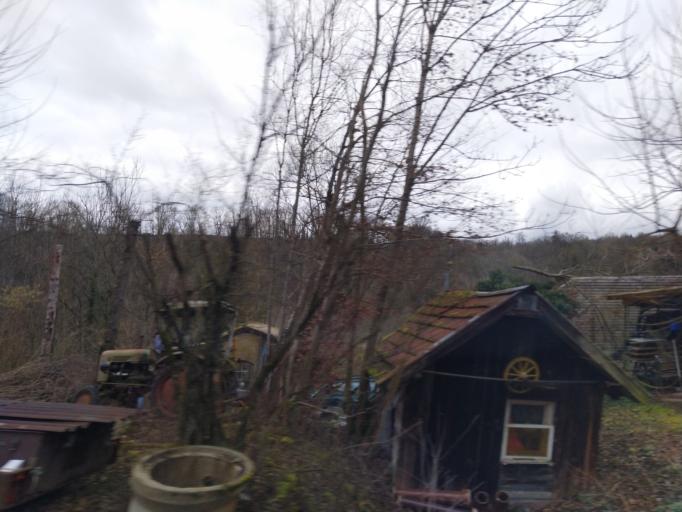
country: DE
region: Baden-Wuerttemberg
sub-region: Regierungsbezirk Stuttgart
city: Burgstetten
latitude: 48.9319
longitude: 9.3568
